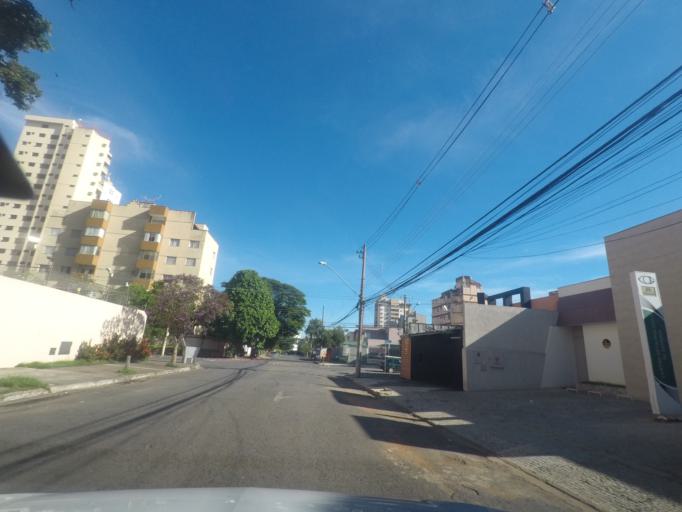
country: BR
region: Goias
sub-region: Goiania
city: Goiania
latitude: -16.6752
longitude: -49.2702
